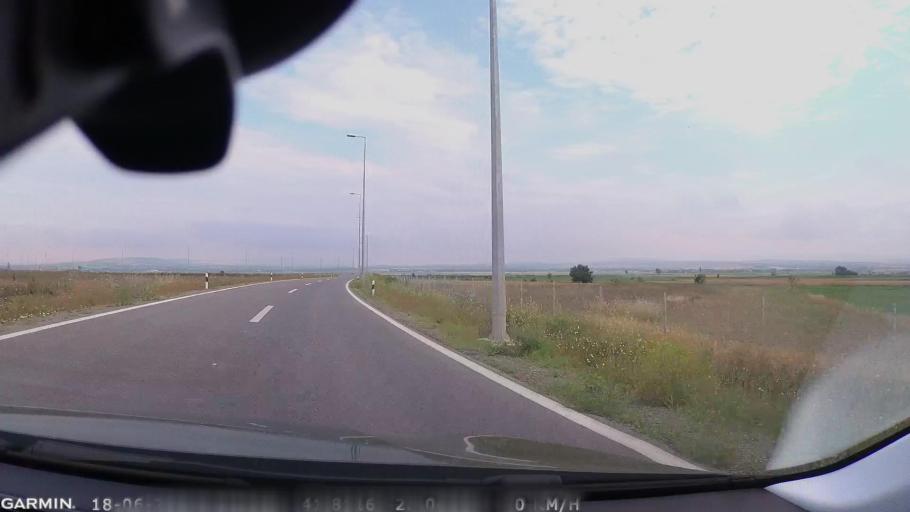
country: MK
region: Sveti Nikole
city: Sveti Nikole
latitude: 41.8116
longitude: 22.0420
